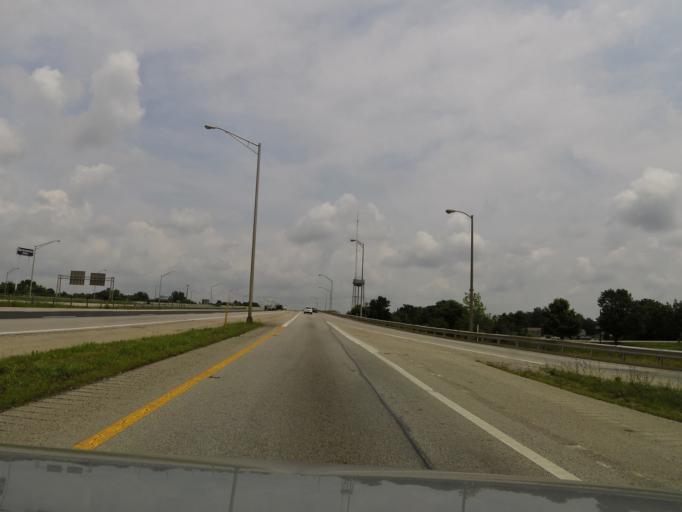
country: US
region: Kentucky
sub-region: Hardin County
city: Elizabethtown
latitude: 37.6760
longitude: -85.8482
